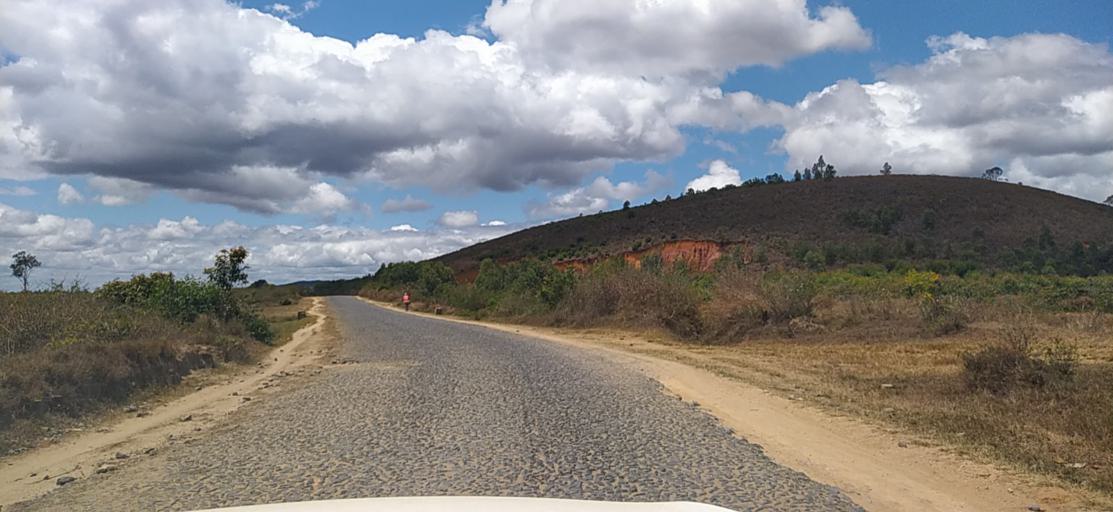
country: MG
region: Alaotra Mangoro
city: Moramanga
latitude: -18.7586
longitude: 48.2583
